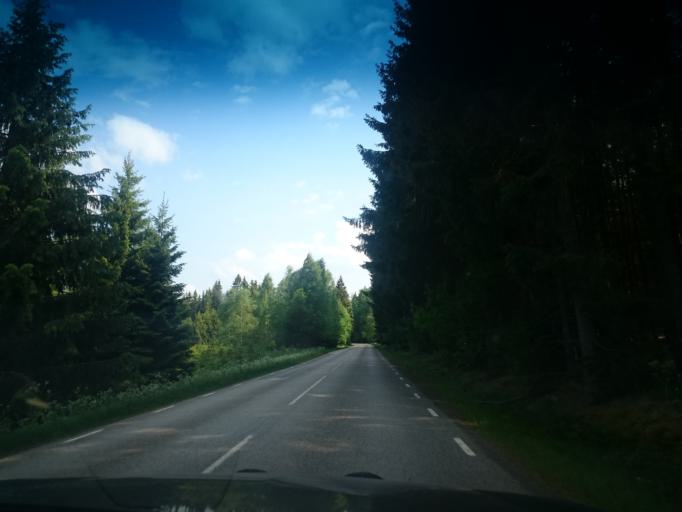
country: SE
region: Joenkoeping
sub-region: Vetlanda Kommun
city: Vetlanda
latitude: 57.3667
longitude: 15.0577
